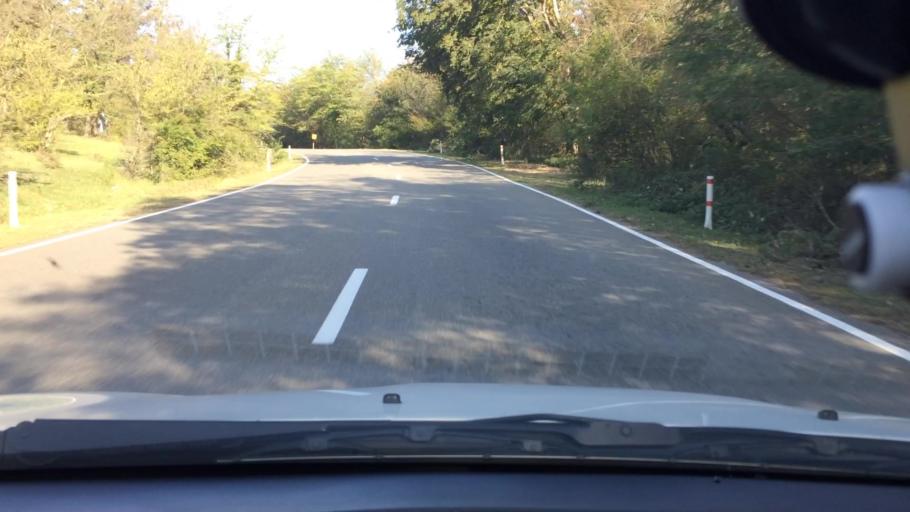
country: GE
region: Imereti
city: Kutaisi
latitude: 42.2496
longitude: 42.7547
